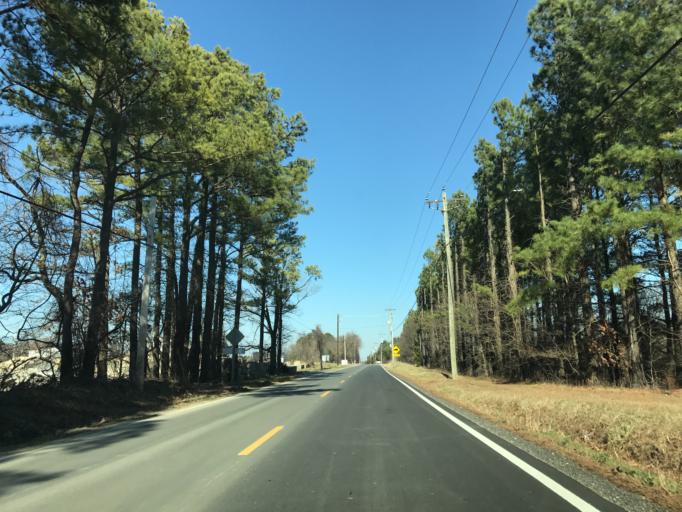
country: US
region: Maryland
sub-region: Queen Anne's County
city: Centreville
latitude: 39.0018
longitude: -76.1361
